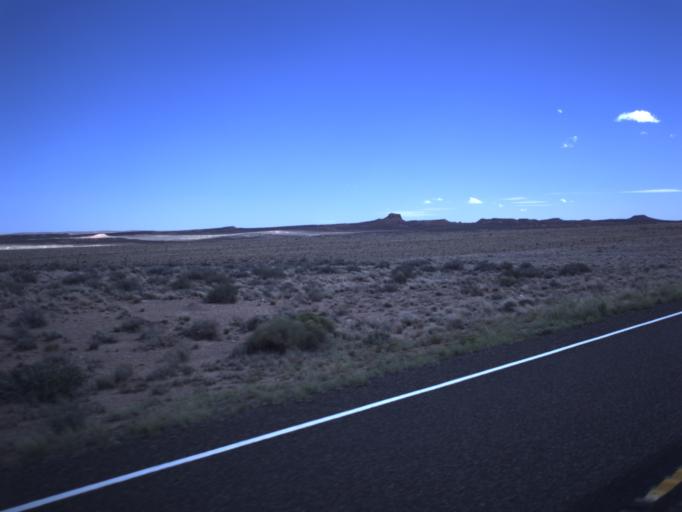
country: US
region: Utah
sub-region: Emery County
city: Ferron
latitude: 38.2841
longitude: -110.6636
